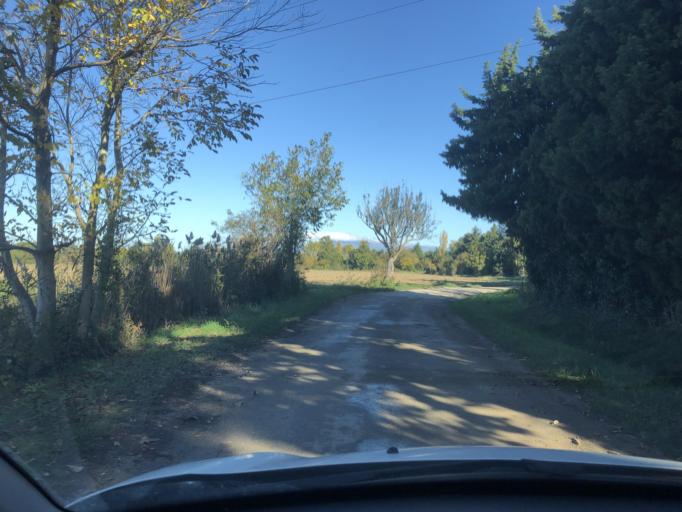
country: FR
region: Provence-Alpes-Cote d'Azur
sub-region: Departement du Vaucluse
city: Althen-des-Paluds
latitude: 43.9890
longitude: 4.9986
